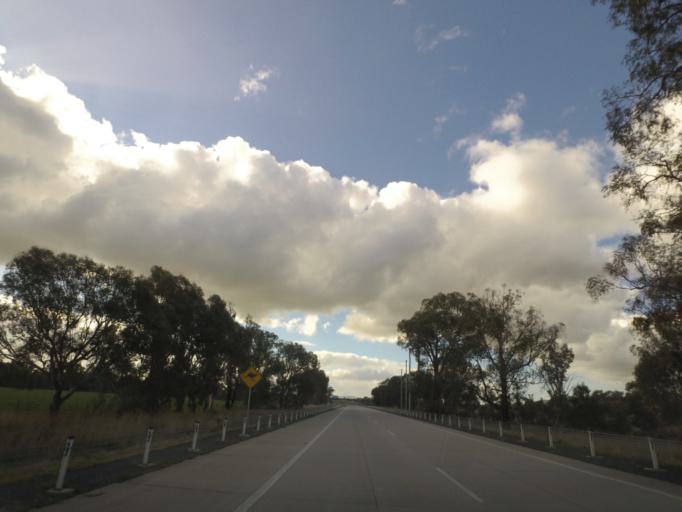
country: AU
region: New South Wales
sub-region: Greater Hume Shire
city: Holbrook
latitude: -35.7417
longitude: 147.3021
